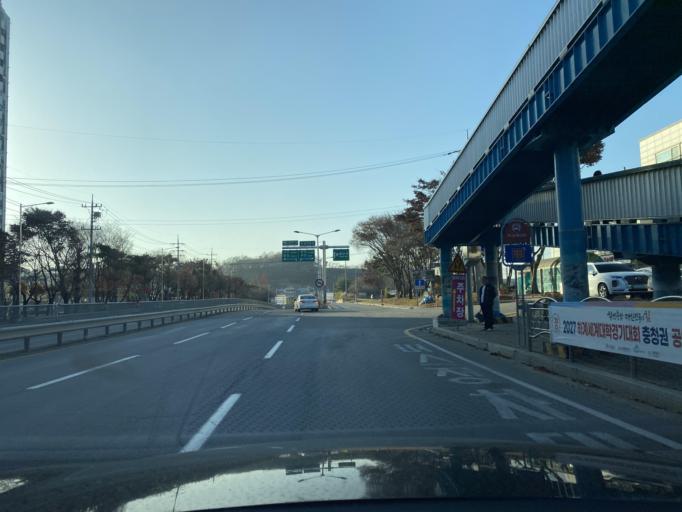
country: KR
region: Chungcheongnam-do
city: Yesan
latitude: 36.6939
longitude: 126.8324
